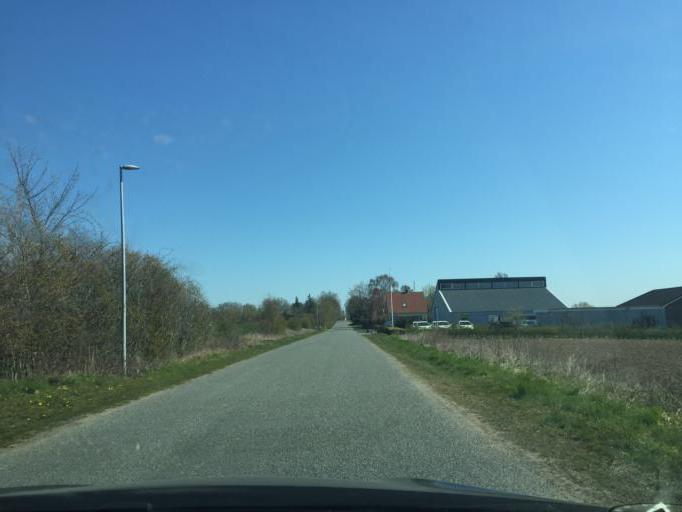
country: DK
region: South Denmark
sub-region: Faaborg-Midtfyn Kommune
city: Ringe
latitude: 55.2464
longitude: 10.4940
